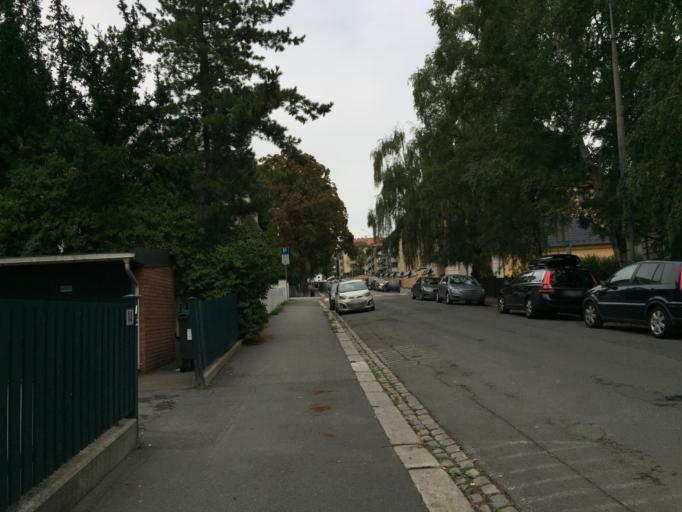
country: NO
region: Oslo
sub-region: Oslo
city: Sjolyststranda
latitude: 59.9141
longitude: 10.7076
